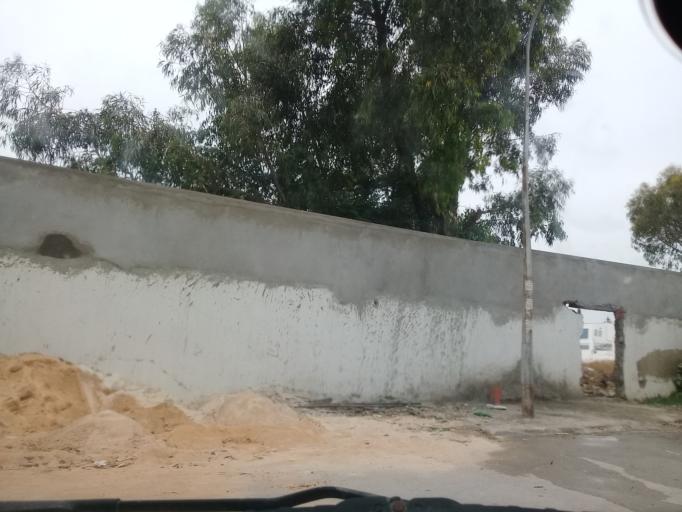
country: TN
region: Tunis
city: Tunis
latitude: 36.8404
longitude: 10.1639
